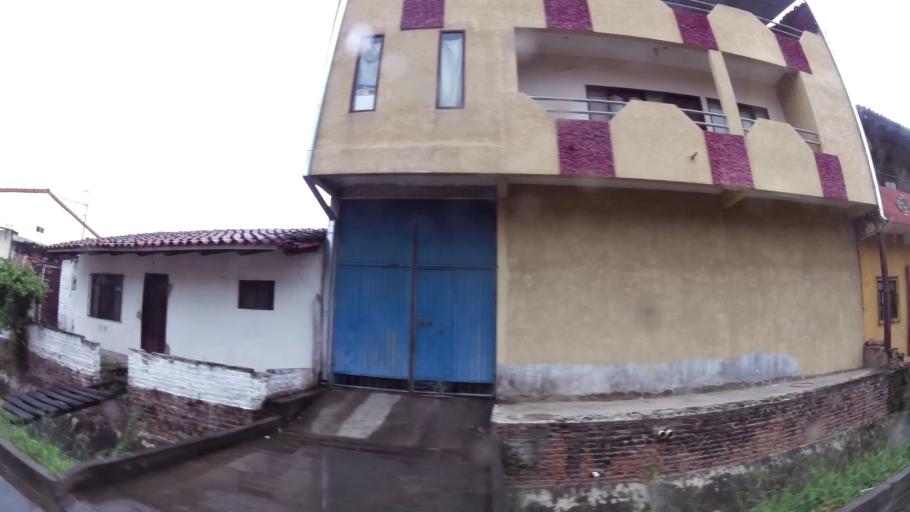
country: BO
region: Santa Cruz
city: Santa Cruz de la Sierra
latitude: -17.7924
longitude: -63.1616
